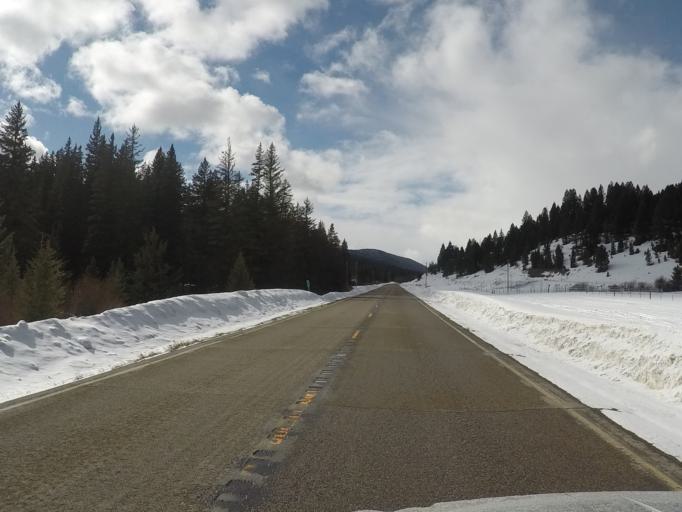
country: US
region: Montana
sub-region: Meagher County
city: White Sulphur Springs
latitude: 46.7606
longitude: -110.7482
